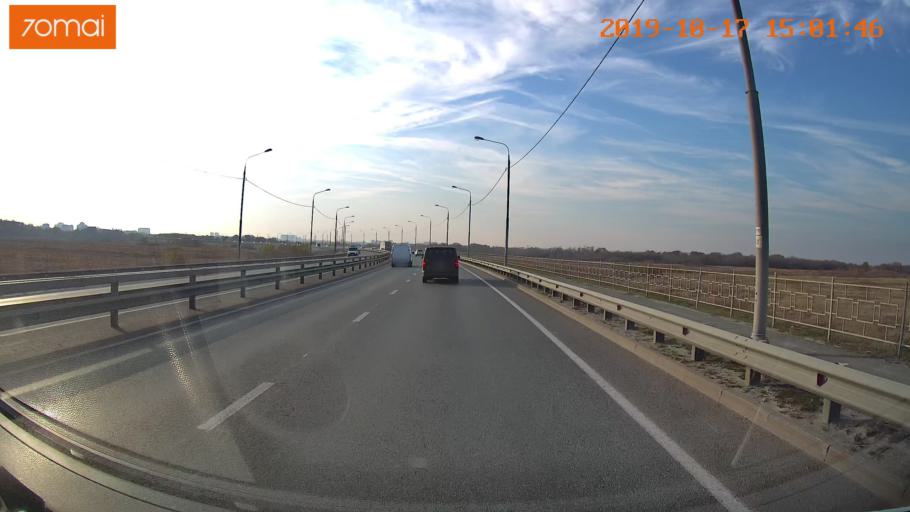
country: RU
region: Rjazan
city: Ryazan'
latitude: 54.6475
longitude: 39.7516
